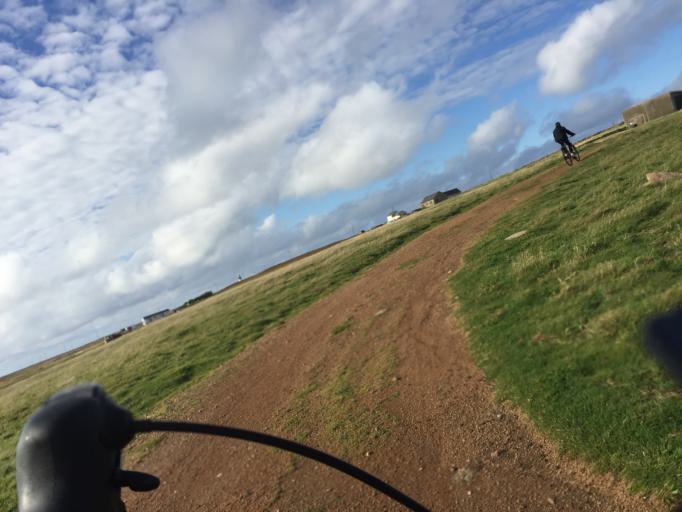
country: IE
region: Ulster
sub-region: County Donegal
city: Derrybeg
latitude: 55.2628
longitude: -8.2341
